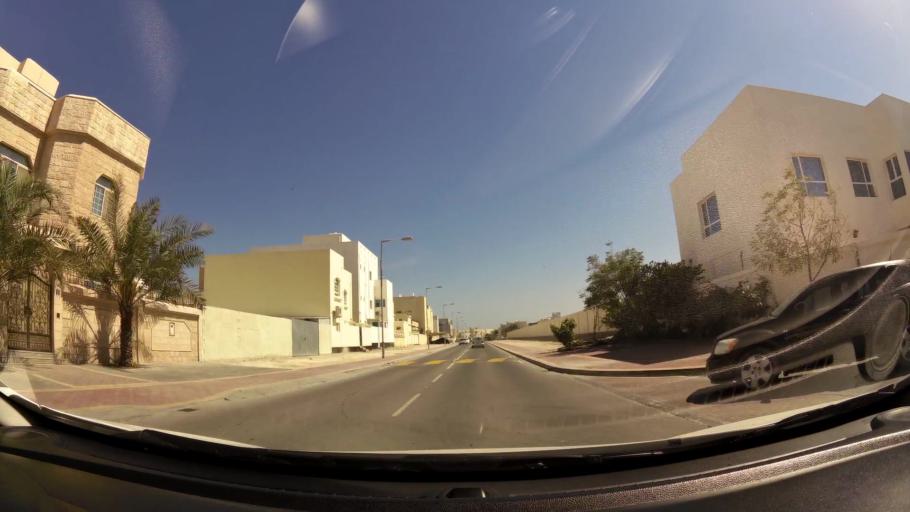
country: BH
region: Muharraq
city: Al Hadd
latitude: 26.2749
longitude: 50.6537
